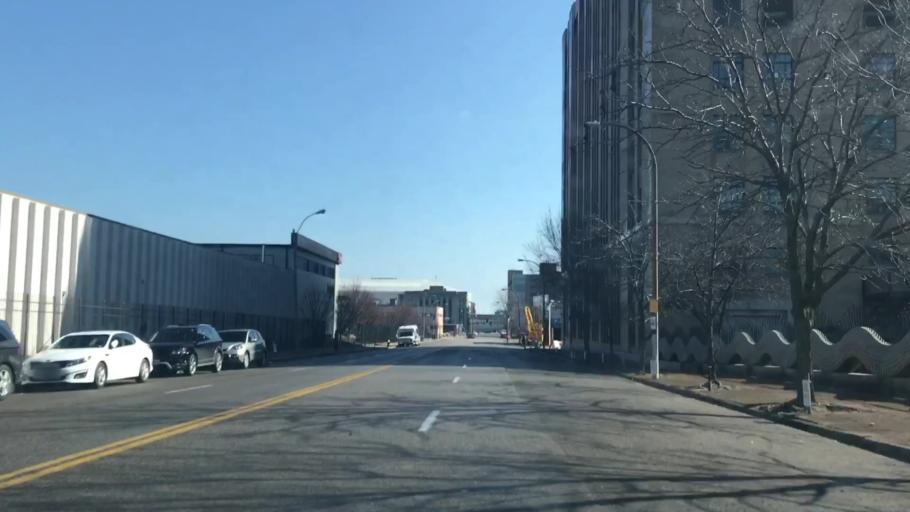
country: US
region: Missouri
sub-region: City of Saint Louis
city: St. Louis
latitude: 38.6343
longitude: -90.2012
